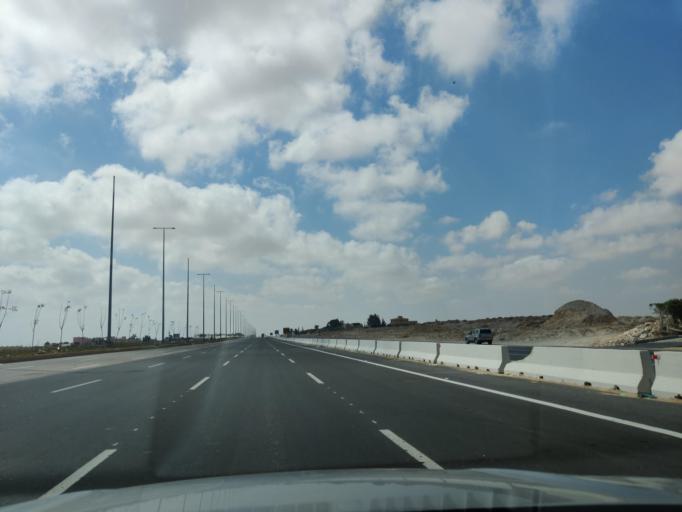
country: EG
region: Muhafazat Matruh
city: Al `Alamayn
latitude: 30.9349
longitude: 28.7880
